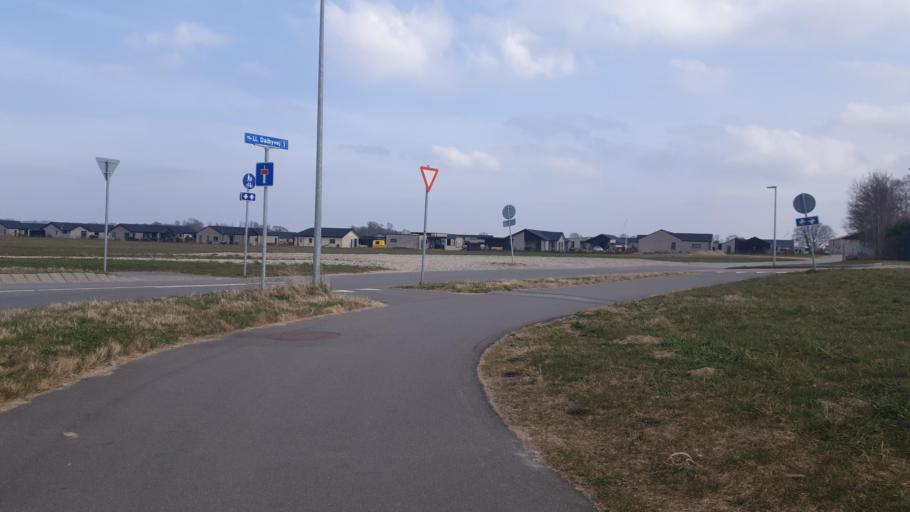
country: DK
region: Central Jutland
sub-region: Hedensted Kommune
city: Hedensted
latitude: 55.7630
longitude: 9.7242
